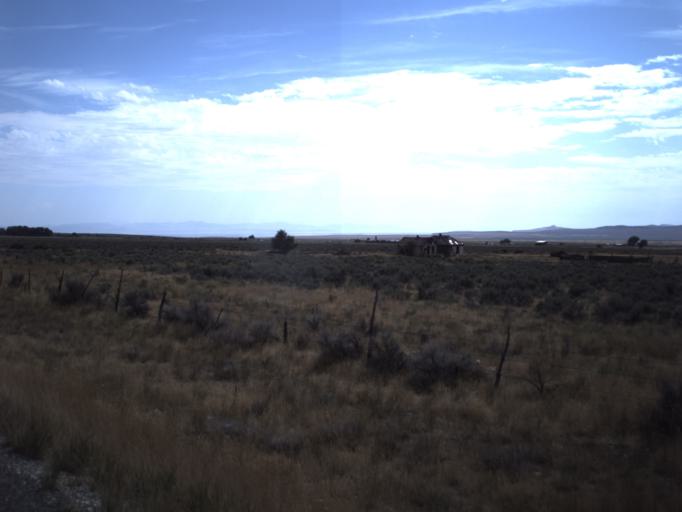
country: US
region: Idaho
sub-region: Cassia County
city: Burley
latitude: 41.8167
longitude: -113.3514
